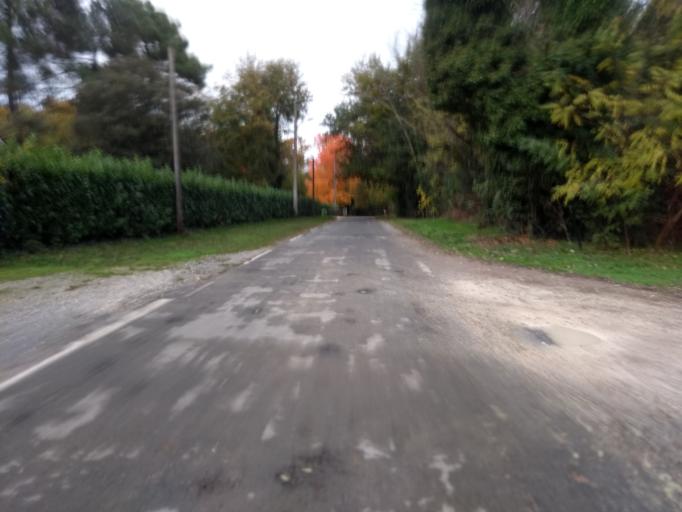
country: FR
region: Aquitaine
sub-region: Departement de la Gironde
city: Gradignan
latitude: 44.7609
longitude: -0.6045
